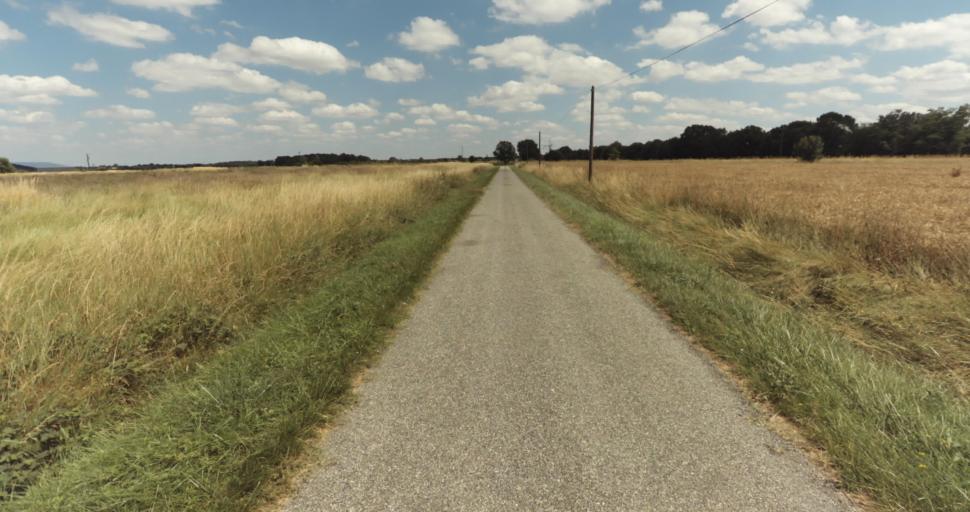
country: FR
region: Midi-Pyrenees
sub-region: Departement de la Haute-Garonne
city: Fontenilles
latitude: 43.5645
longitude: 1.1739
